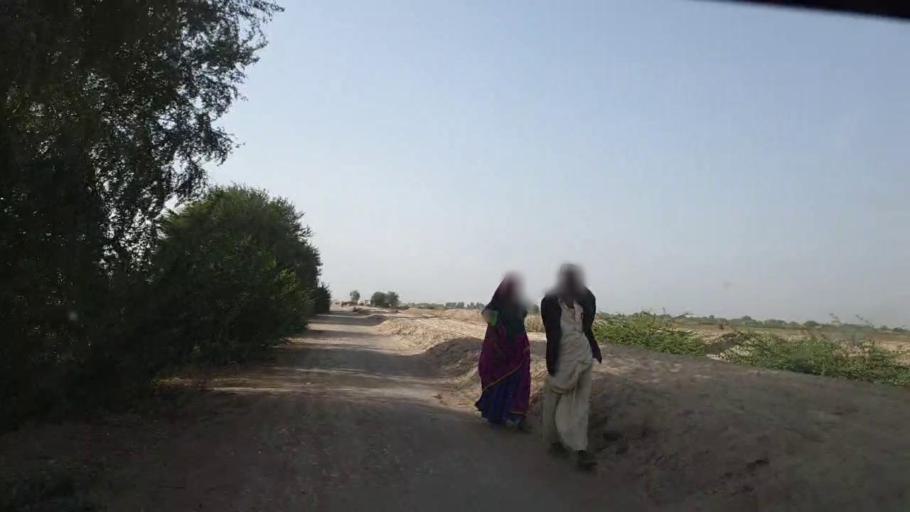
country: PK
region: Sindh
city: Naukot
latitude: 24.9843
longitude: 69.4881
